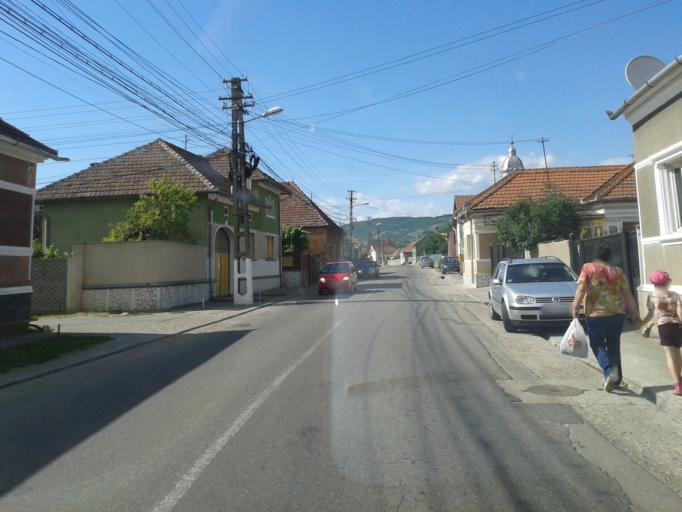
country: RO
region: Hunedoara
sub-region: Comuna Geoagiu
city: Geoagiu
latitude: 45.9110
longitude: 23.2065
